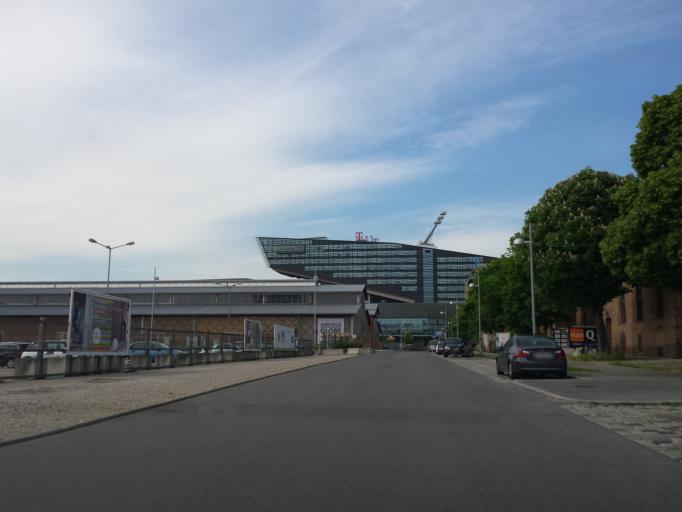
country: AT
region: Vienna
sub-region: Wien Stadt
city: Vienna
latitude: 48.1893
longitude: 16.4061
